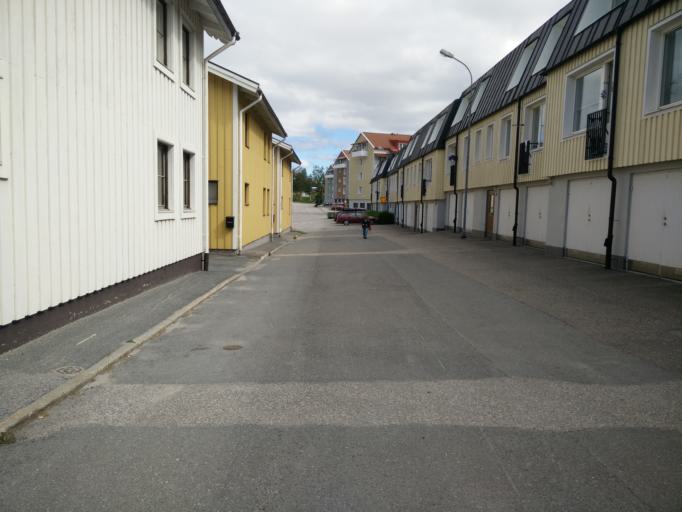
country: SE
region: Vaesternorrland
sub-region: Haernoesands Kommun
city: Haernoesand
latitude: 62.6377
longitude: 17.9463
